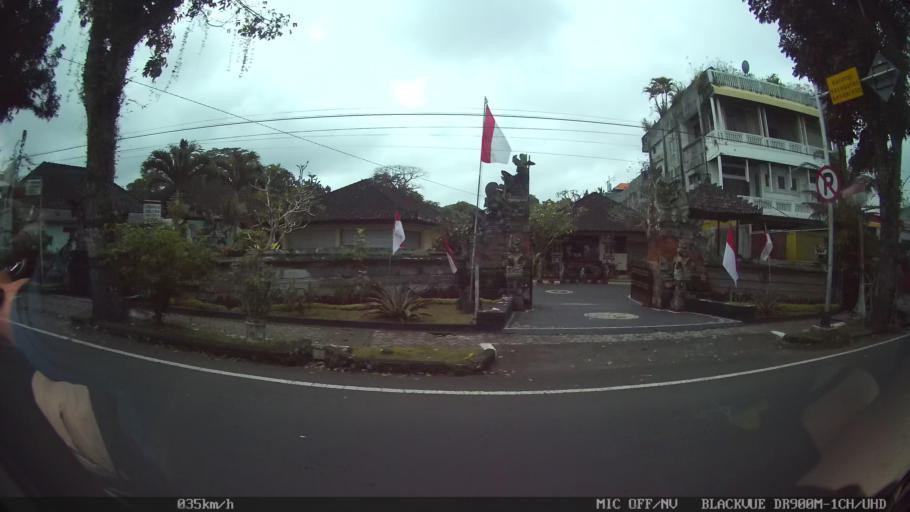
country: ID
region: Bali
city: Banjar Bebalang
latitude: -8.4663
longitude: 115.3526
